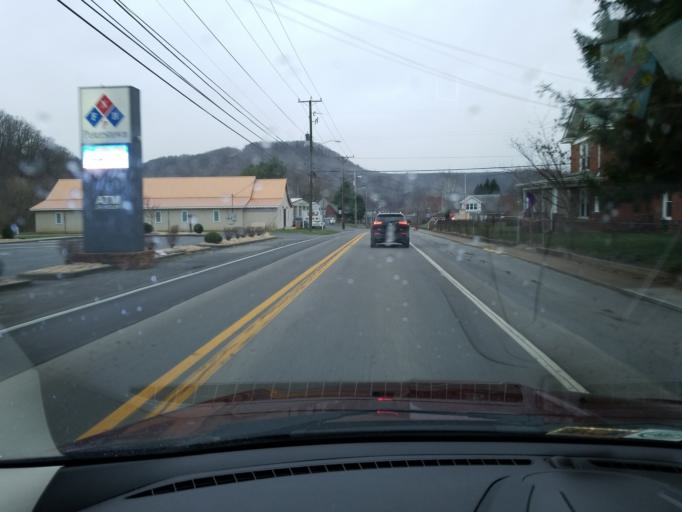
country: US
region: Virginia
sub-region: Giles County
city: Narrows
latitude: 37.3960
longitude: -80.7942
